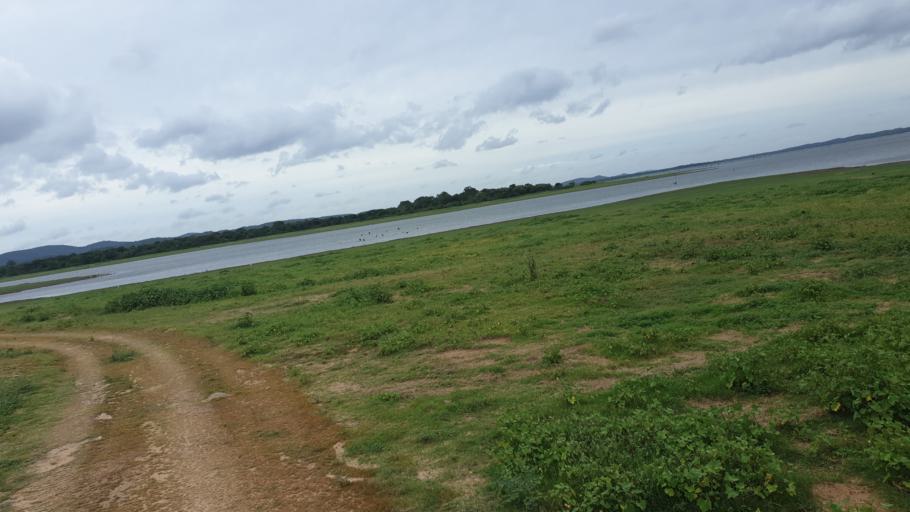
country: LK
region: North Central
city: Polonnaruwa
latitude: 8.1318
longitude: 80.9126
